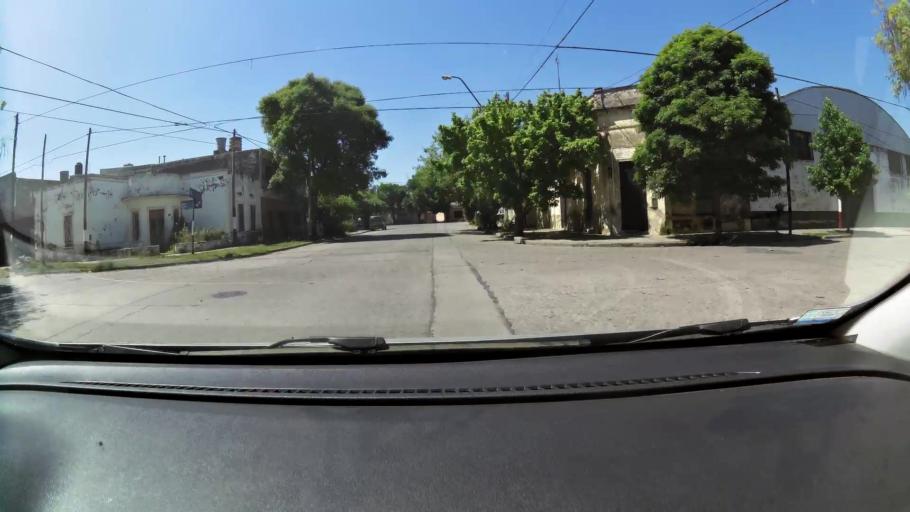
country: AR
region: Cordoba
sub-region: Departamento de Capital
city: Cordoba
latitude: -31.3878
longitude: -64.1913
